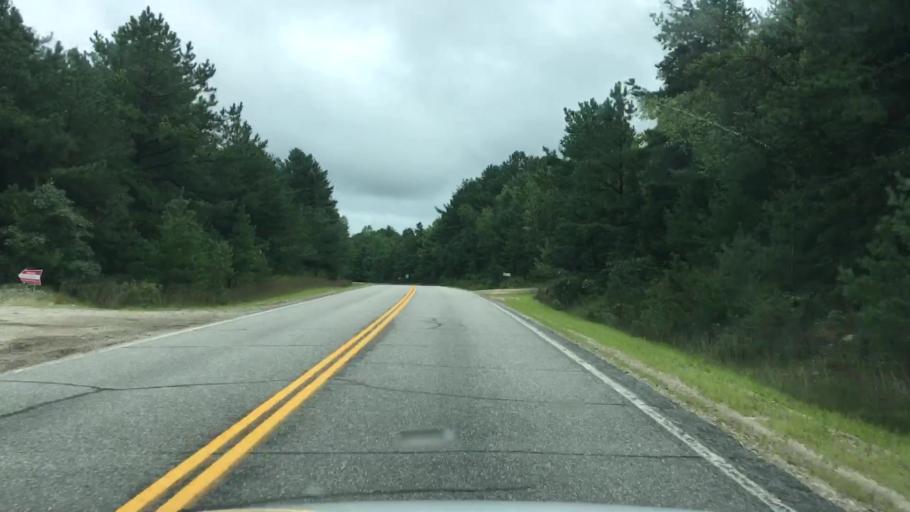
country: US
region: Maine
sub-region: Oxford County
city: Hiram
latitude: 43.9055
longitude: -70.8450
